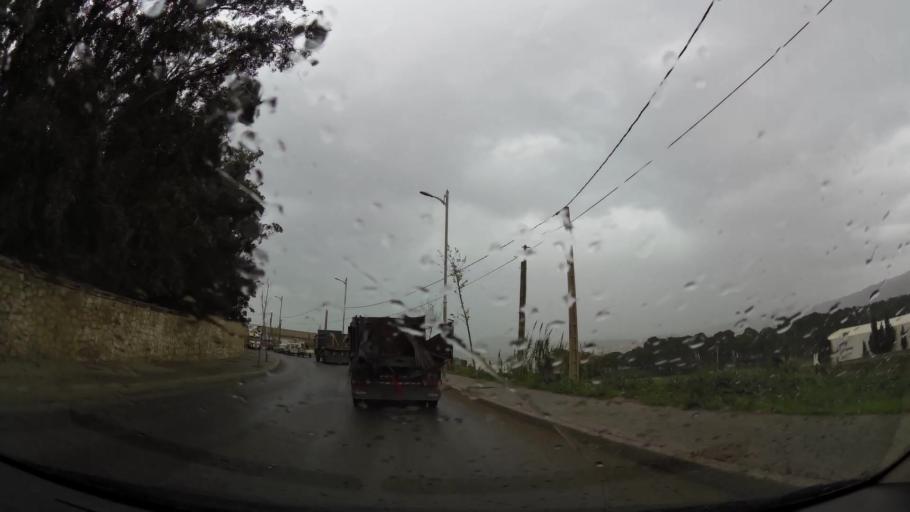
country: MA
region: Tanger-Tetouan
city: Tetouan
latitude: 35.5571
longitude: -5.4047
